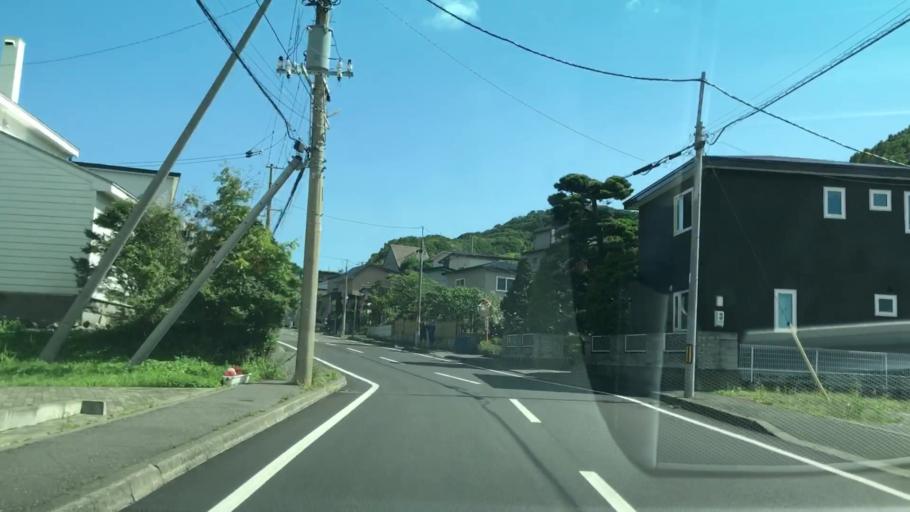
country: JP
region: Hokkaido
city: Muroran
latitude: 42.3092
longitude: 140.9984
